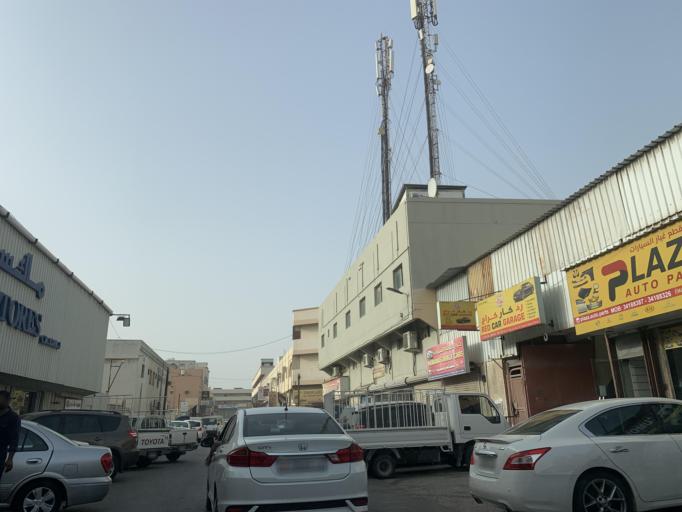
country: BH
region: Northern
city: Madinat `Isa
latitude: 26.1845
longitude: 50.5313
